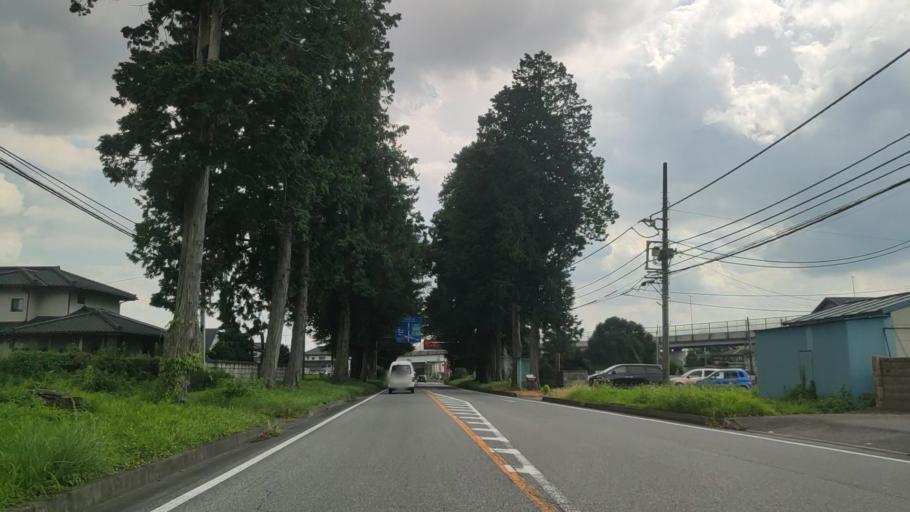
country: JP
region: Tochigi
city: Utsunomiya-shi
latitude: 36.6273
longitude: 139.8520
